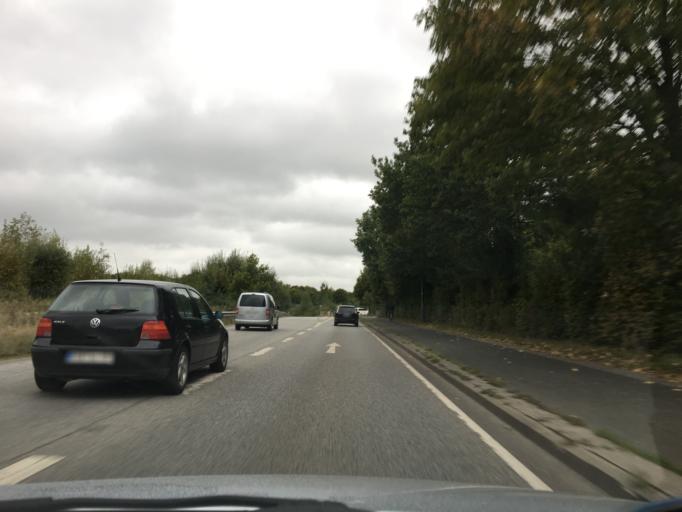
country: DE
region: Schleswig-Holstein
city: Altenholz
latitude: 54.3625
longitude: 10.1256
